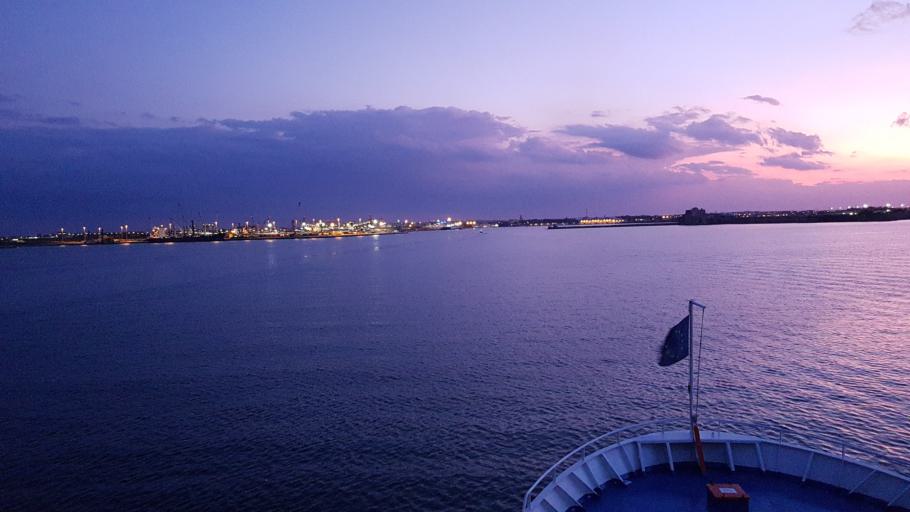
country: IT
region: Apulia
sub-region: Provincia di Brindisi
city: Materdomini
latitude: 40.6584
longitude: 17.9843
